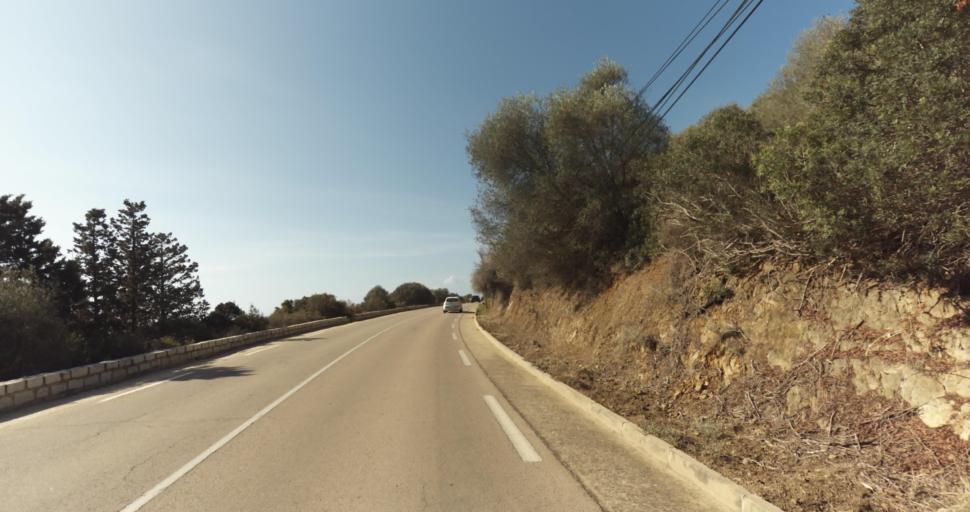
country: FR
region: Corsica
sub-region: Departement de la Corse-du-Sud
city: Ajaccio
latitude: 41.9053
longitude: 8.6270
